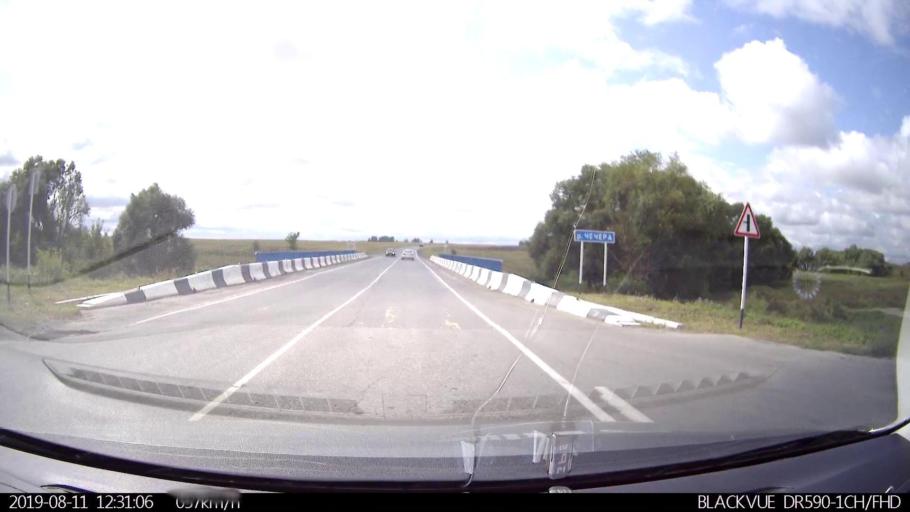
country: RU
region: Ulyanovsk
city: Ignatovka
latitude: 53.8214
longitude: 47.8880
